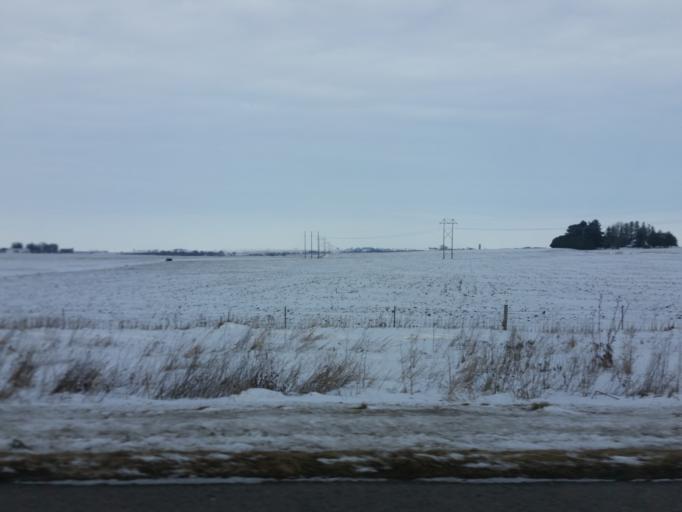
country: US
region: Iowa
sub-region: Delaware County
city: Manchester
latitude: 42.4643
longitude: -91.5709
